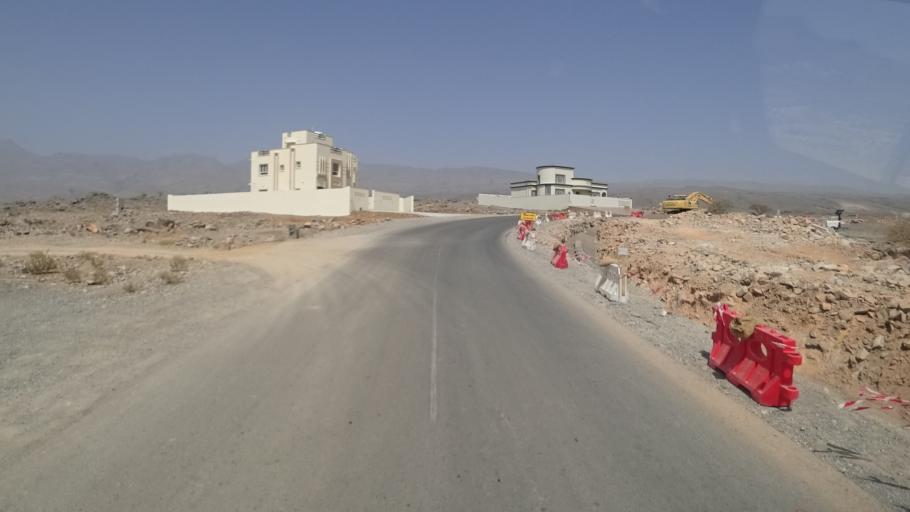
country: OM
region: Muhafazat ad Dakhiliyah
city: Bahla'
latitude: 23.0902
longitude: 57.3234
